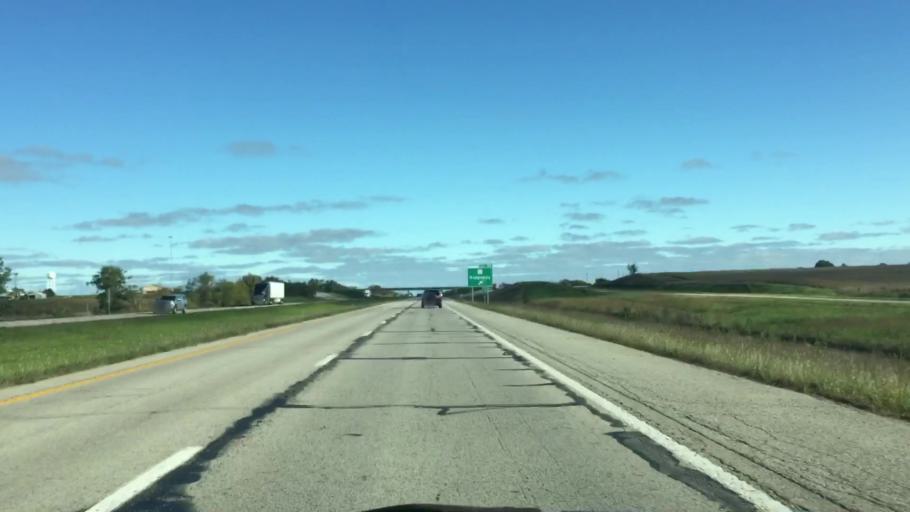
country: US
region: Missouri
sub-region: Harrison County
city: Bethany
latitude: 40.3679
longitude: -94.0045
